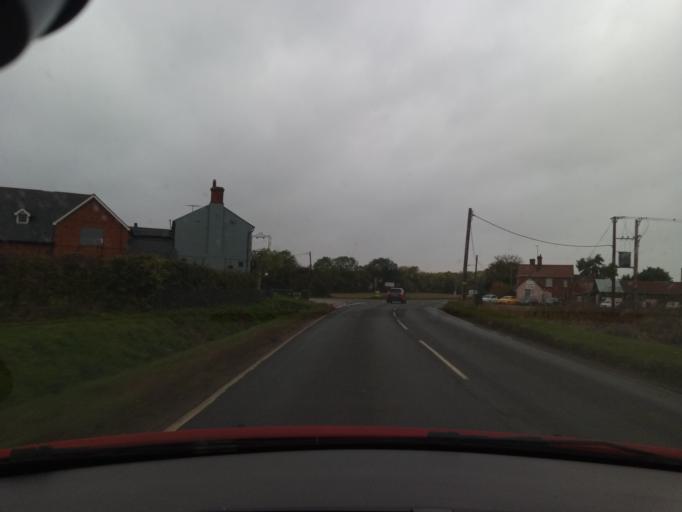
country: GB
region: England
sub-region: Suffolk
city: Kedington
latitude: 52.0559
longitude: 0.4936
